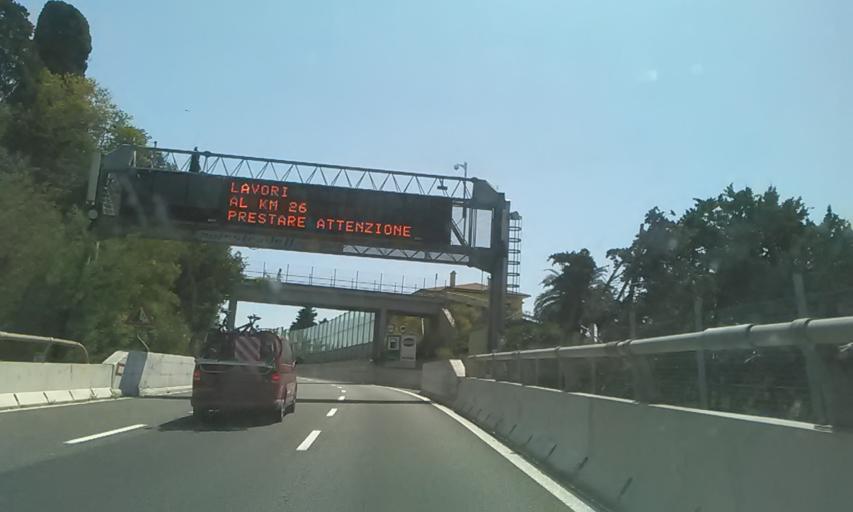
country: IT
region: Liguria
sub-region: Provincia di Savona
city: Varazze
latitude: 44.3624
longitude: 8.5904
